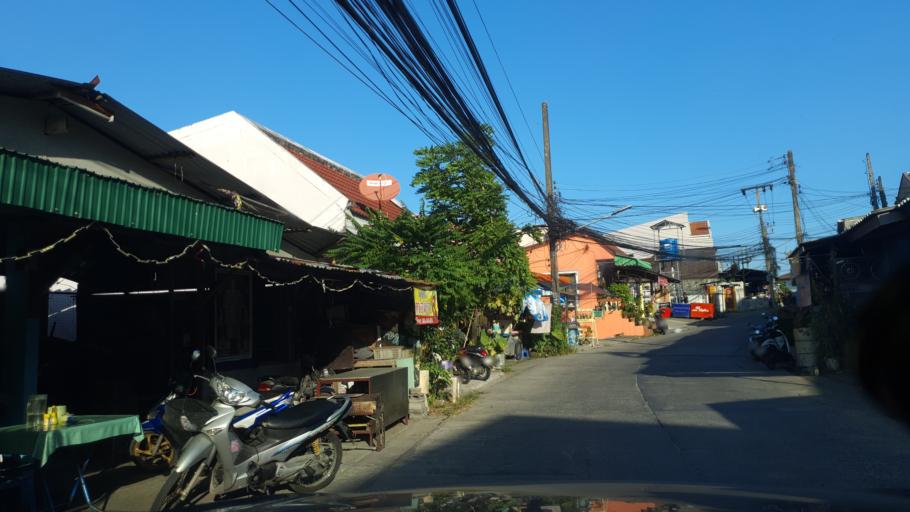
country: TH
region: Phuket
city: Kathu
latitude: 7.9029
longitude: 98.3312
